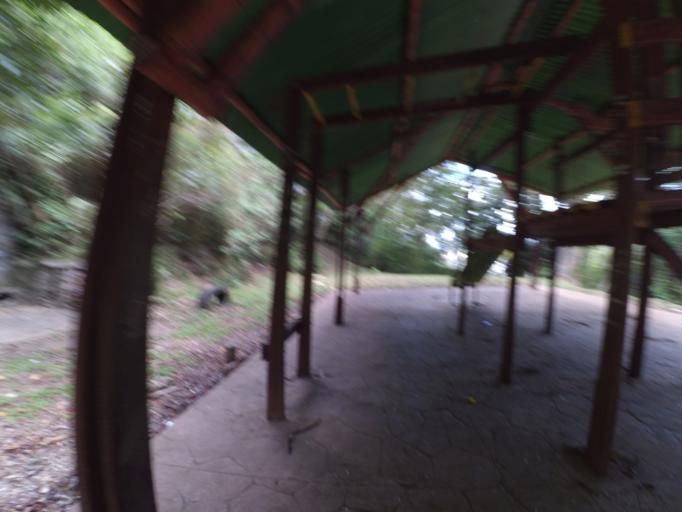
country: CO
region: Cauca
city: Popayan
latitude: 2.4432
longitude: -76.5986
